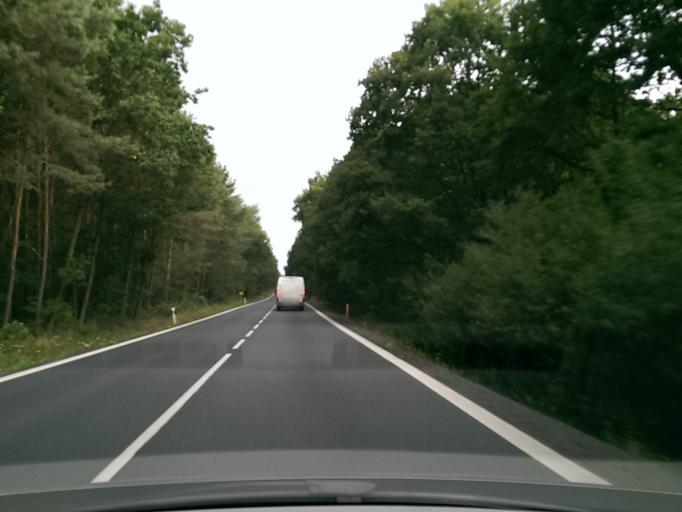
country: CZ
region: Central Bohemia
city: Loucen
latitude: 50.2603
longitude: 14.9798
